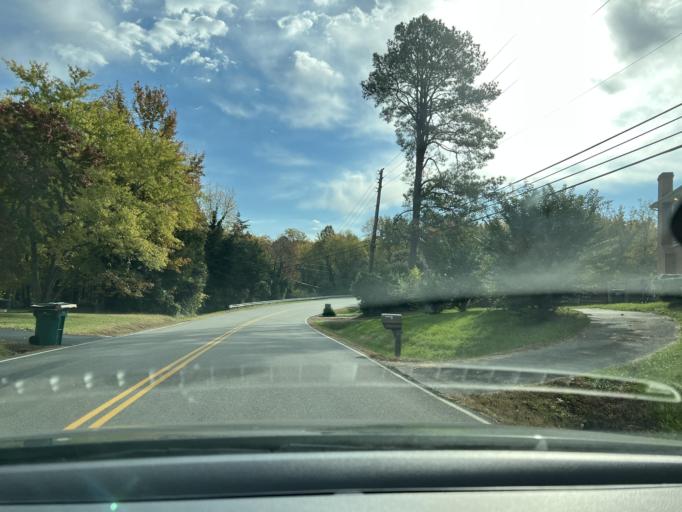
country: US
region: Virginia
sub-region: Henrico County
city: Tuckahoe
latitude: 37.6122
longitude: -77.5401
